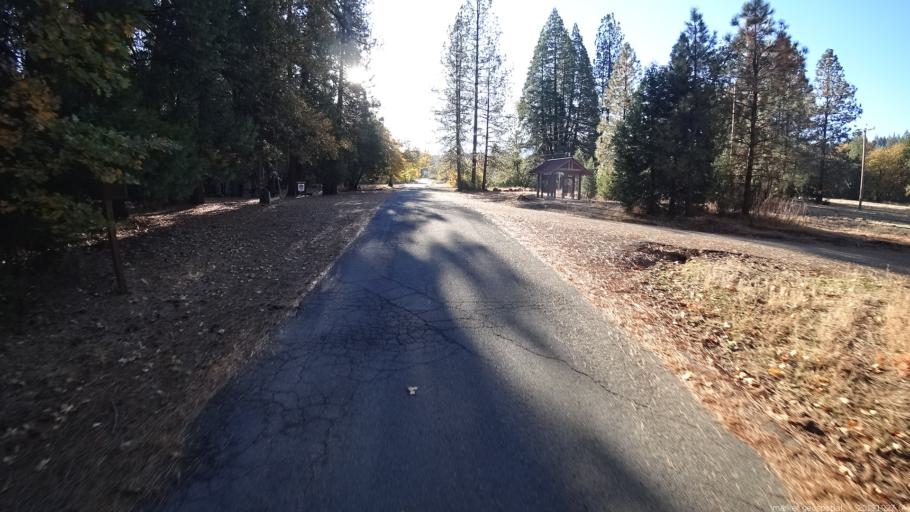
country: US
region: California
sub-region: Shasta County
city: Burney
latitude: 41.0030
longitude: -121.8911
